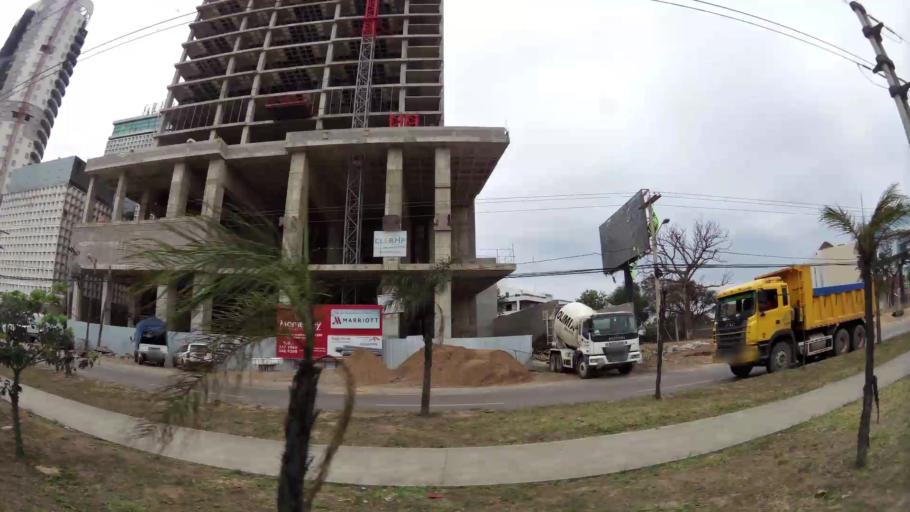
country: BO
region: Santa Cruz
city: Santa Cruz de la Sierra
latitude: -17.7615
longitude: -63.2027
